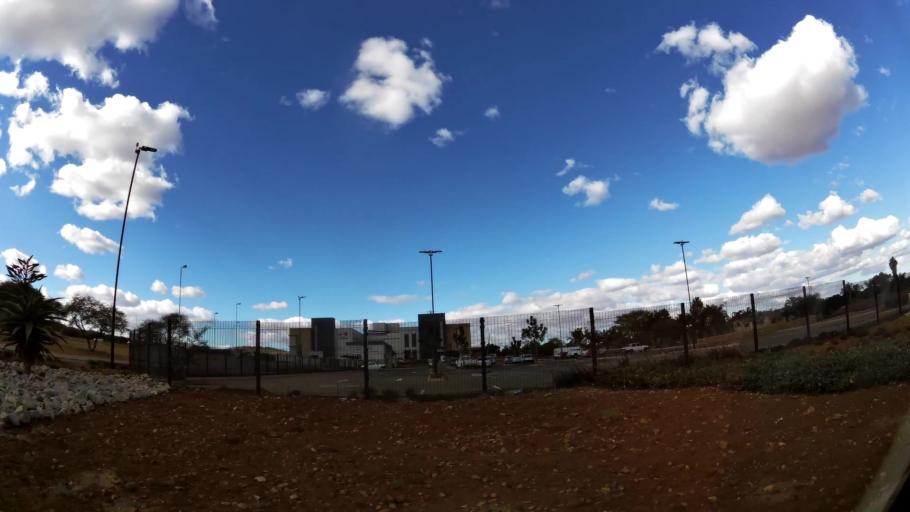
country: ZA
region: Limpopo
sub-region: Capricorn District Municipality
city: Polokwane
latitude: -23.9026
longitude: 29.4913
